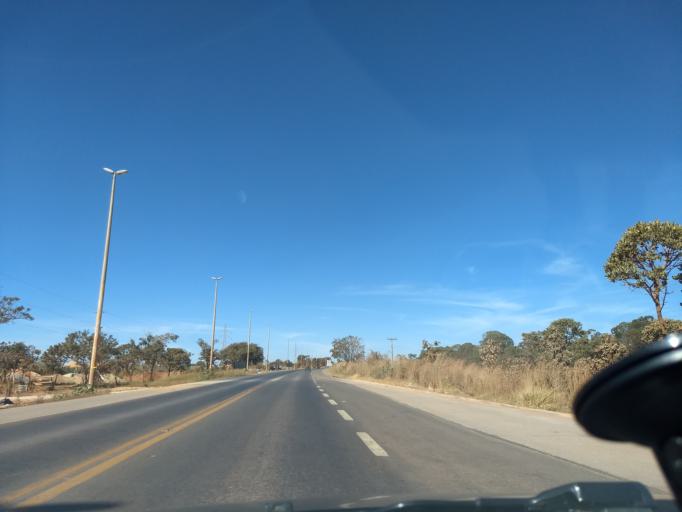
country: BR
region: Federal District
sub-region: Brasilia
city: Brasilia
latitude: -15.7670
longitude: -48.0449
